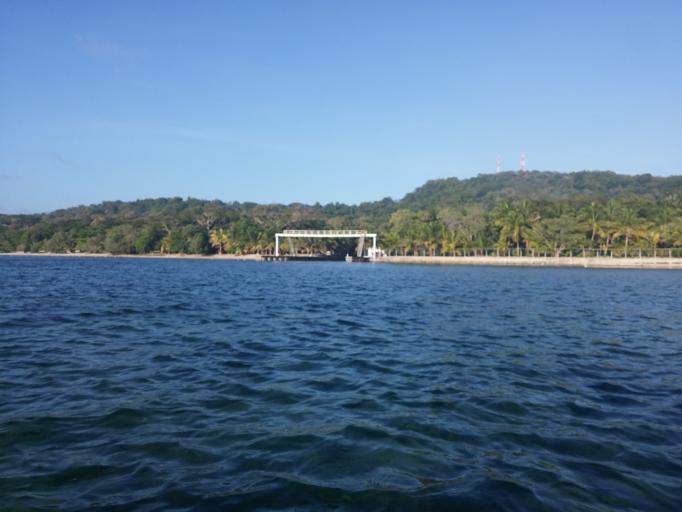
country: HN
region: Bay Islands
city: Sandy Bay
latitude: 16.2827
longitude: -86.6002
